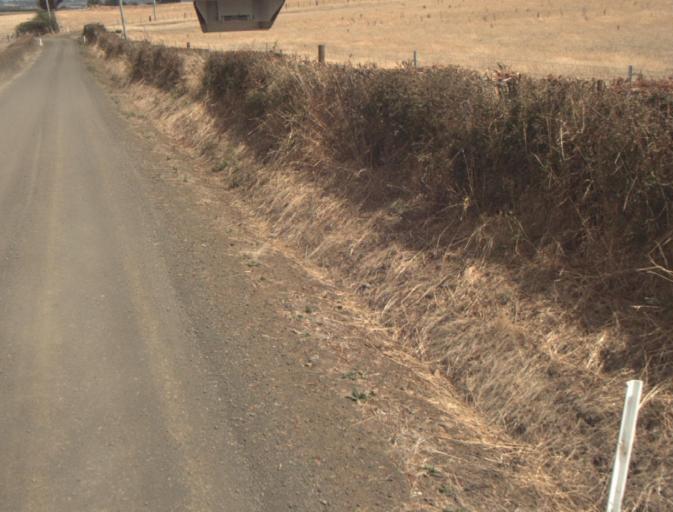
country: AU
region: Tasmania
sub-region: Northern Midlands
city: Evandale
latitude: -41.5206
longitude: 147.2842
